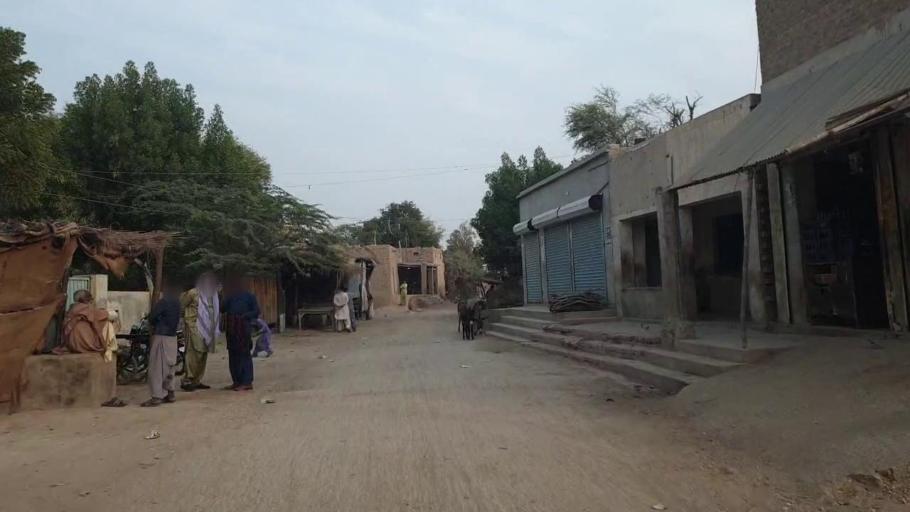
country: PK
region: Sindh
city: Sann
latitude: 26.1719
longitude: 68.0172
